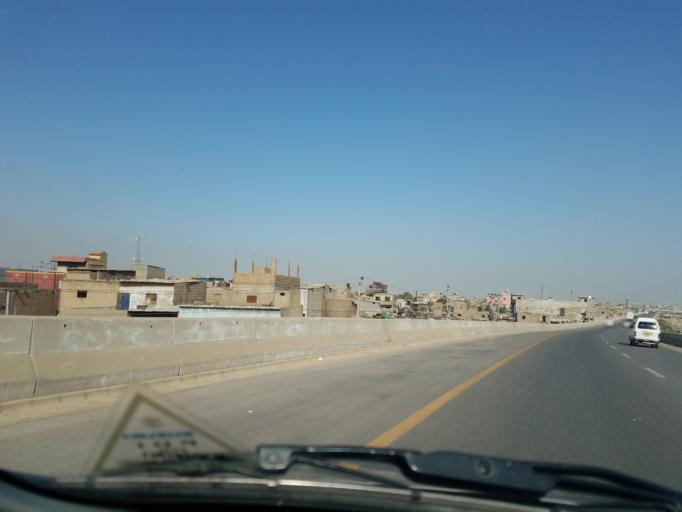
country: PK
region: Sindh
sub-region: Karachi District
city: Karachi
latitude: 24.8820
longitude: 66.9957
